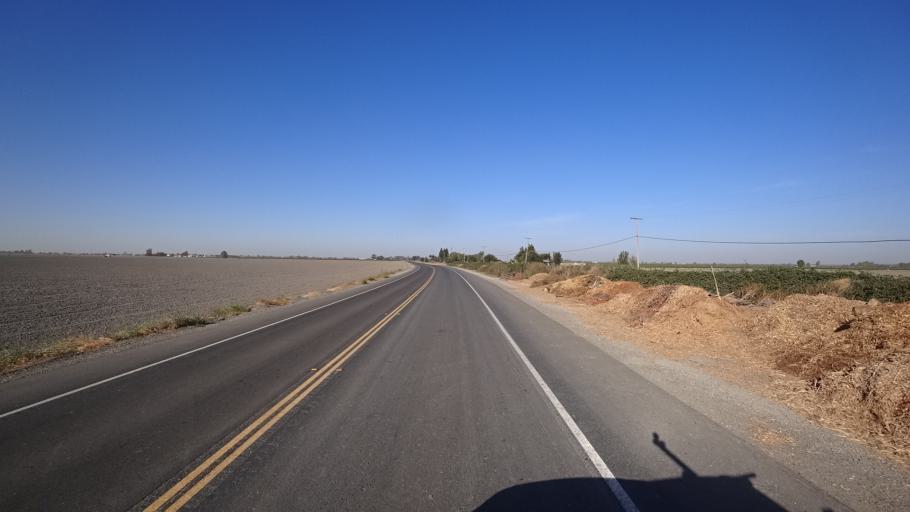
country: US
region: California
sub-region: Sacramento County
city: Parkway
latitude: 38.4146
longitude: -121.5627
